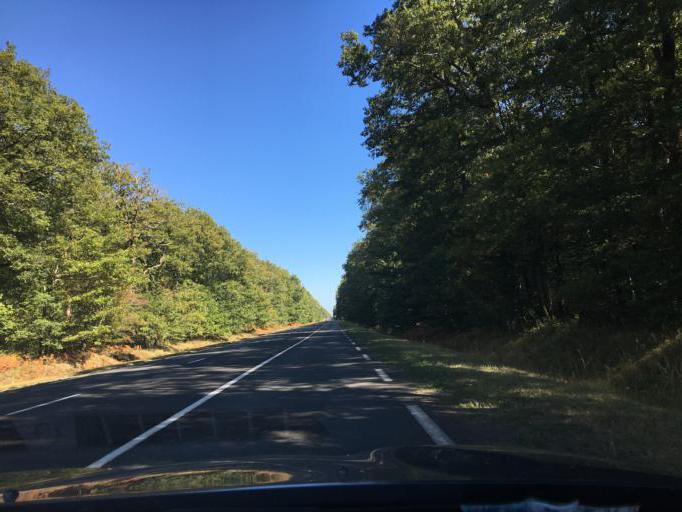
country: FR
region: Centre
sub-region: Departement d'Indre-et-Loire
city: Cheille
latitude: 47.2307
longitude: 0.3999
